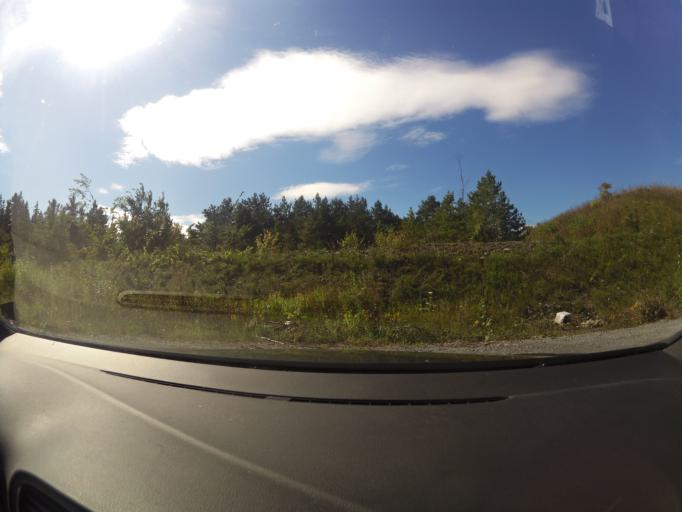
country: CA
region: Ontario
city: Bells Corners
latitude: 45.2184
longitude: -75.9846
